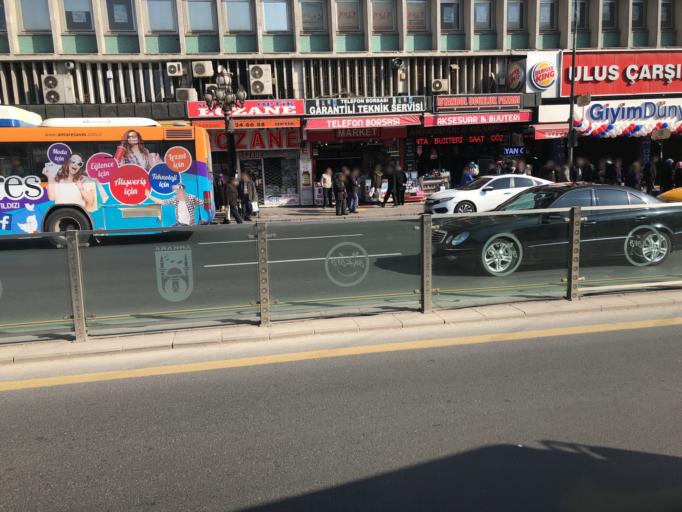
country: TR
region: Ankara
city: Ankara
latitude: 39.9410
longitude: 32.8543
